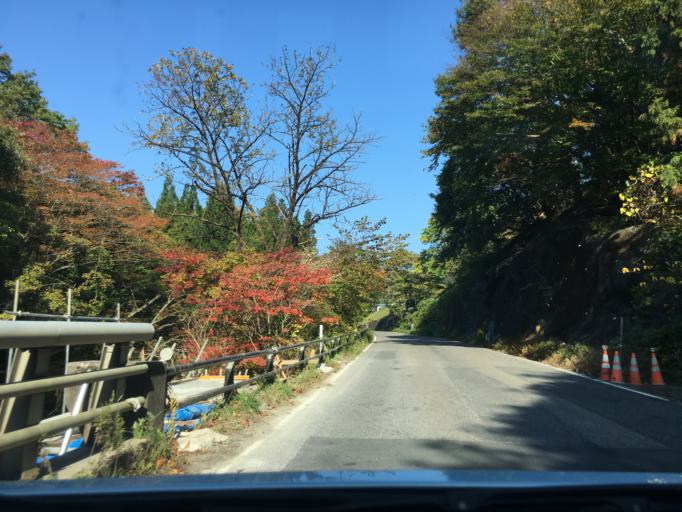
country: JP
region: Fukushima
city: Sukagawa
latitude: 37.3058
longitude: 140.1459
